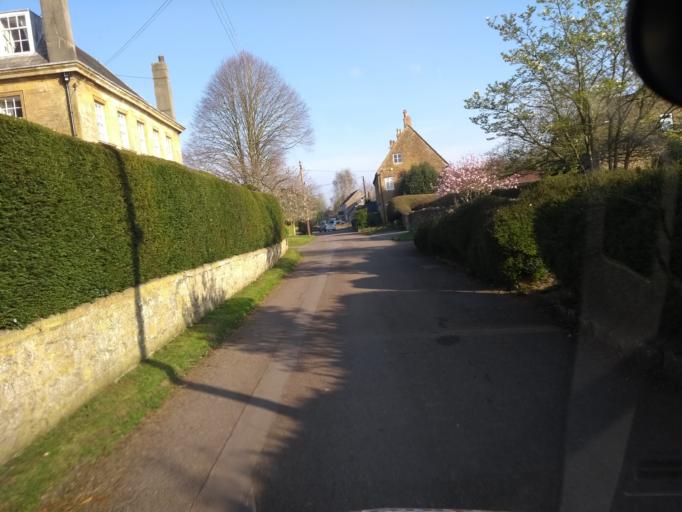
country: GB
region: England
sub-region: Somerset
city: South Petherton
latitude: 50.9337
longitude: -2.8451
